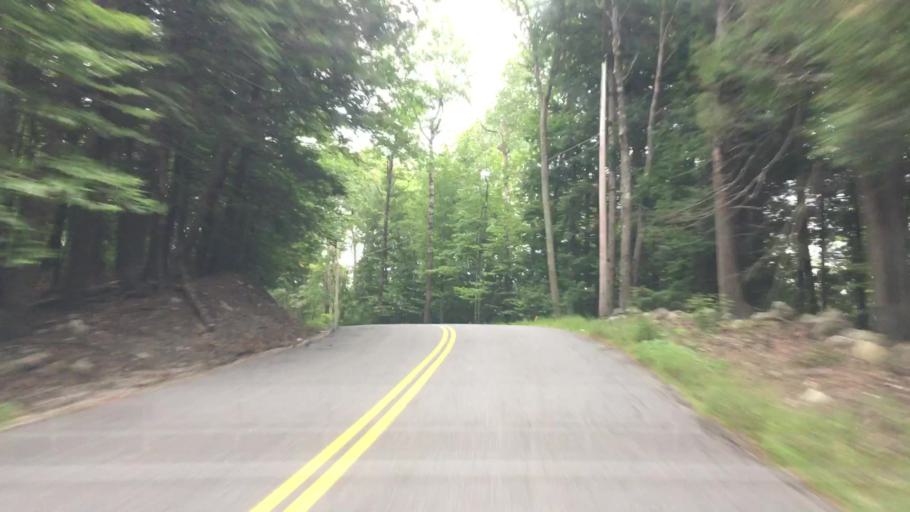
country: US
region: Maine
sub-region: Cumberland County
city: New Gloucester
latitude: 43.9045
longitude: -70.2121
